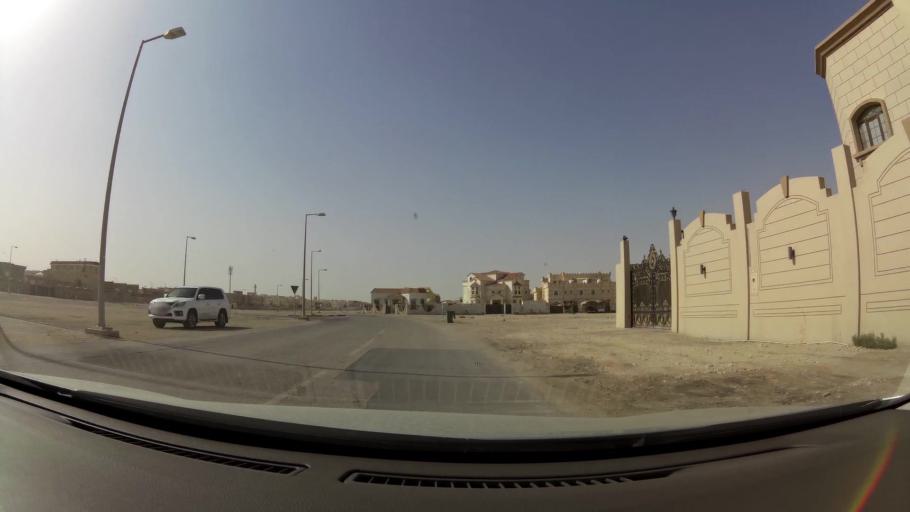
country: QA
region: Baladiyat ar Rayyan
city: Ar Rayyan
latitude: 25.3512
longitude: 51.4492
